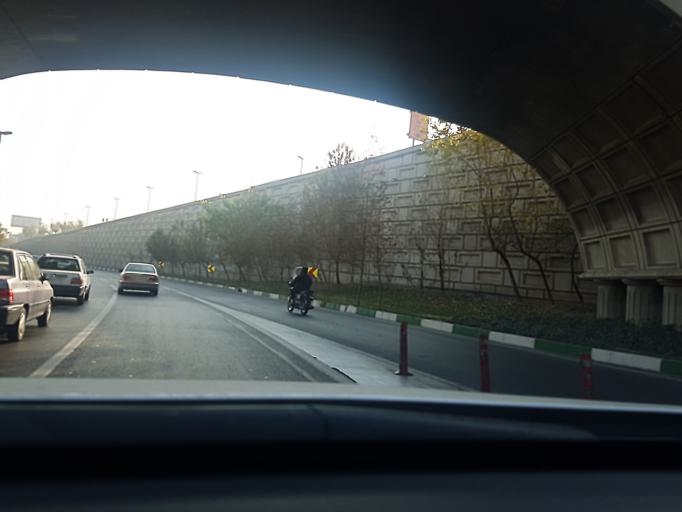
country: IR
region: Tehran
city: Tehran
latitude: 35.7401
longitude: 51.4169
